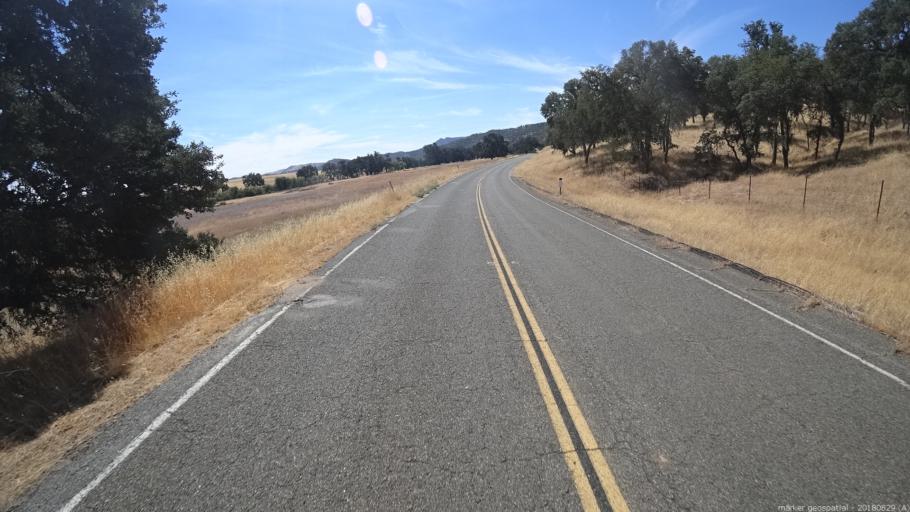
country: US
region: California
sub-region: San Luis Obispo County
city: Lake Nacimiento
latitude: 35.8195
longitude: -121.0083
